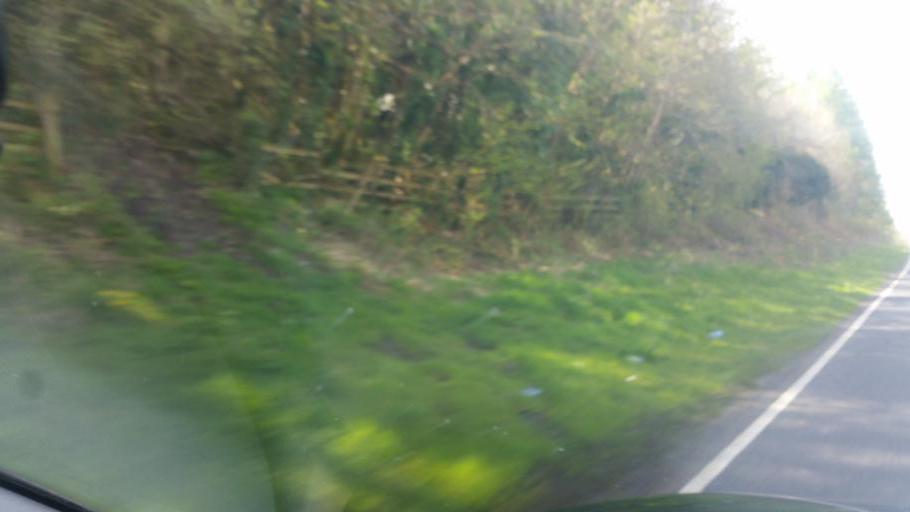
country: GB
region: Northern Ireland
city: Irvinestown
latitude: 54.4205
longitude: -7.7376
